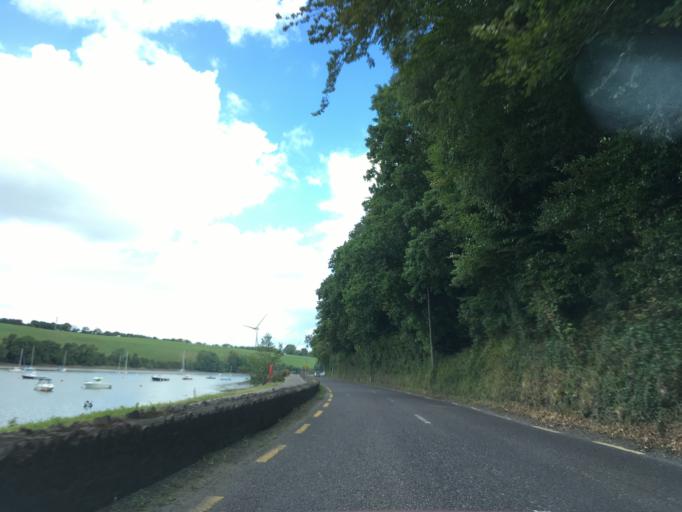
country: IE
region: Munster
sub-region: County Cork
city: Crosshaven
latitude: 51.8034
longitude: -8.3236
